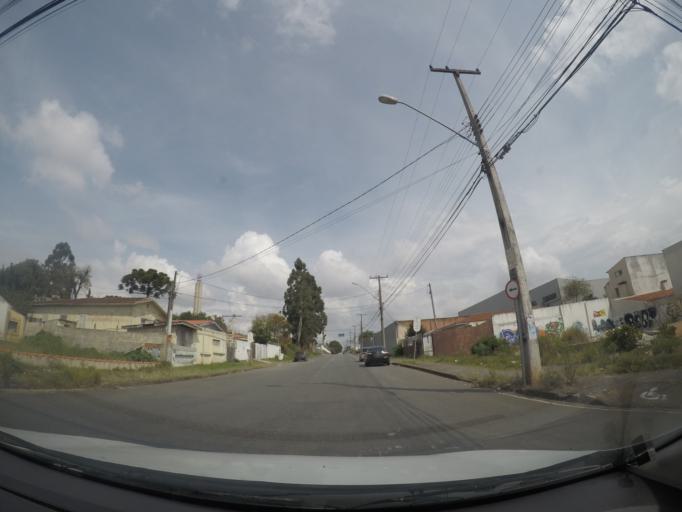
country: BR
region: Parana
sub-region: Curitiba
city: Curitiba
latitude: -25.4837
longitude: -49.2677
